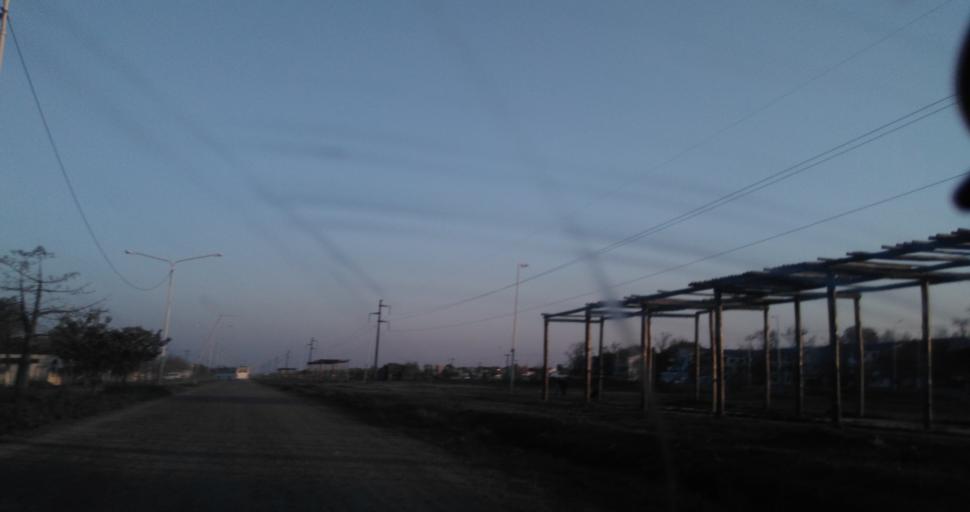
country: AR
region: Chaco
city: Resistencia
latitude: -27.4701
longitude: -59.0099
